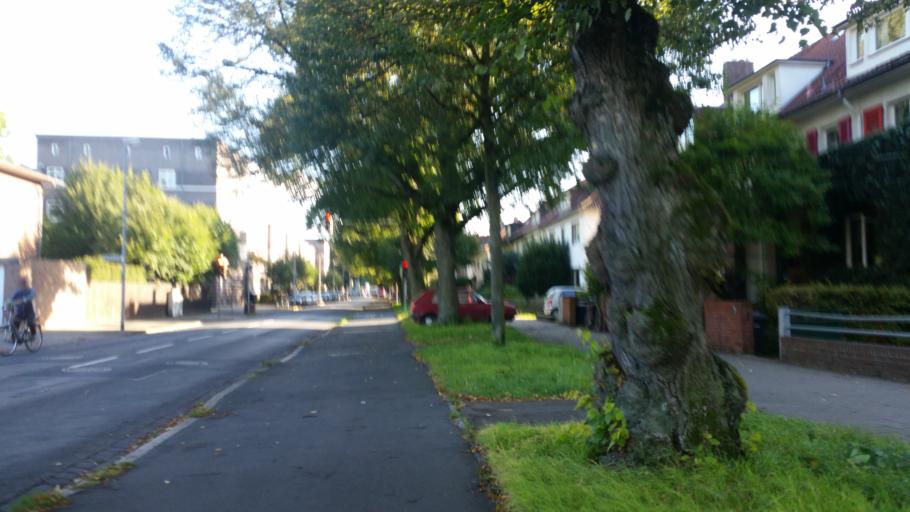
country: DE
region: Lower Saxony
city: Hannover
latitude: 52.4037
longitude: 9.7812
